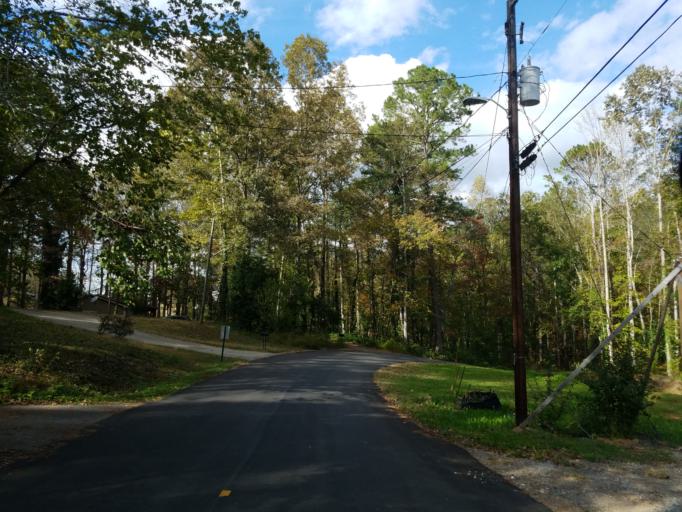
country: US
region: Georgia
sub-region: Pickens County
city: Jasper
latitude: 34.4723
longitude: -84.4299
